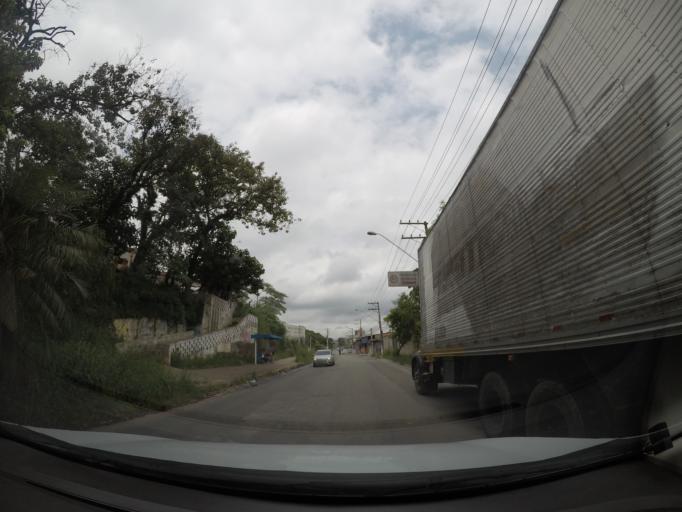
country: BR
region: Sao Paulo
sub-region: Itaquaquecetuba
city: Itaquaquecetuba
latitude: -23.4423
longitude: -46.3905
